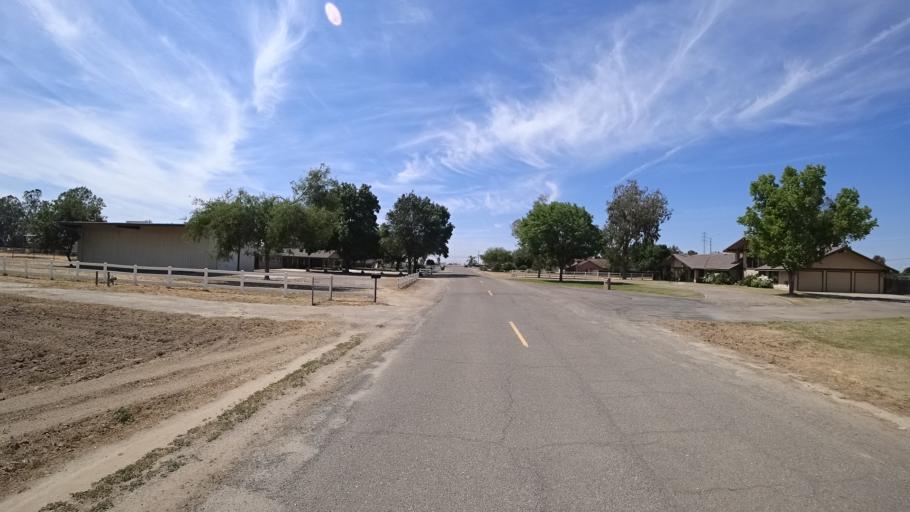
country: US
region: California
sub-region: Kings County
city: Home Garden
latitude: 36.3305
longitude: -119.5899
